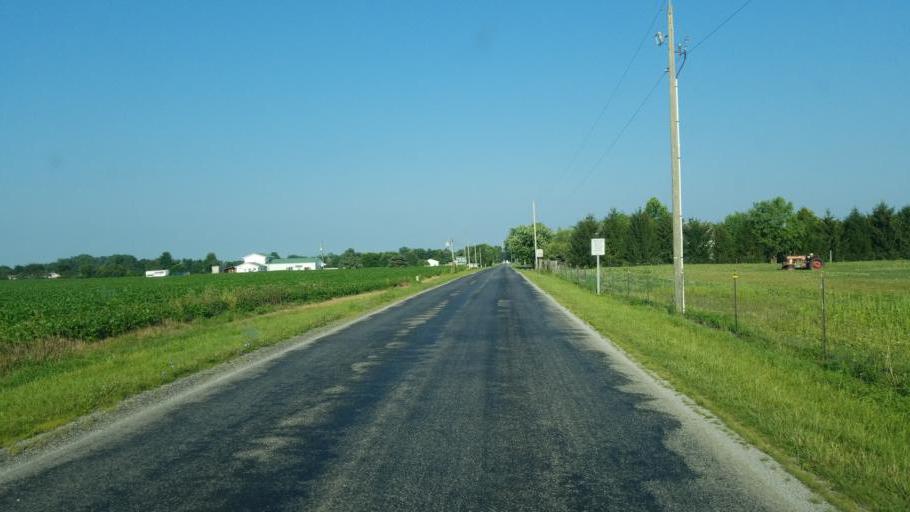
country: US
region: Ohio
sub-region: Hardin County
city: Kenton
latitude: 40.5343
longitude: -83.5076
